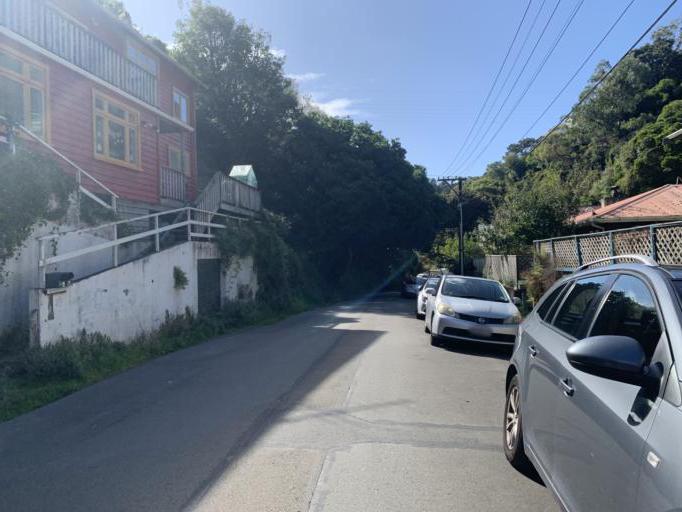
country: NZ
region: Wellington
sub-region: Wellington City
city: Kelburn
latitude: -41.2959
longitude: 174.7576
